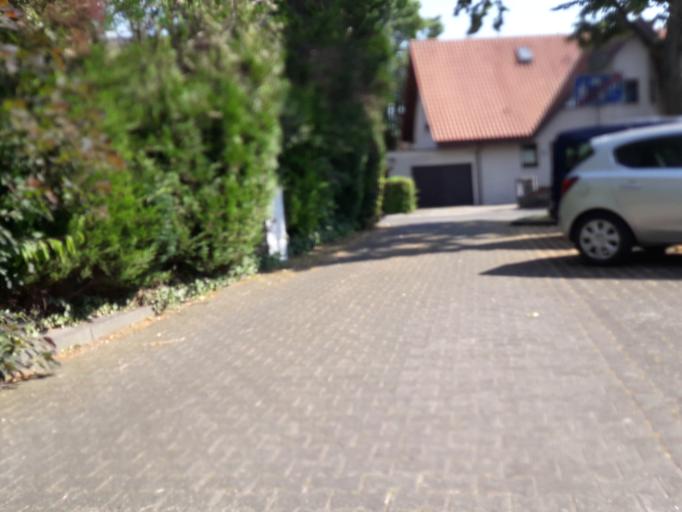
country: DE
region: North Rhine-Westphalia
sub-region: Regierungsbezirk Detmold
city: Paderborn
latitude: 51.7324
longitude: 8.7609
